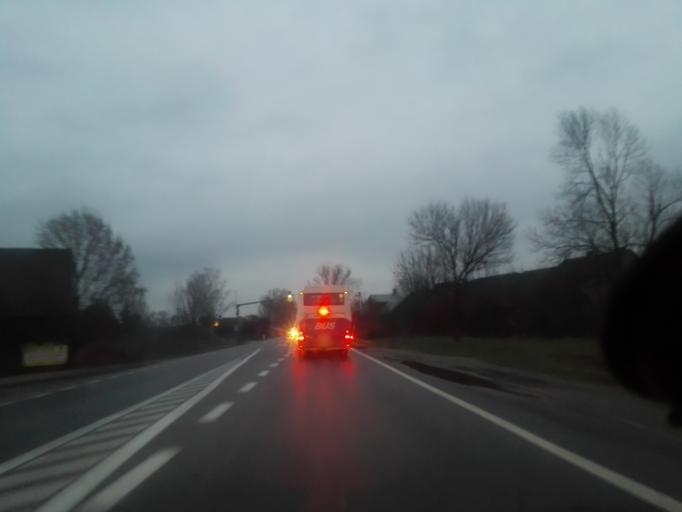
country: PL
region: Masovian Voivodeship
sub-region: Powiat wyszkowski
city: Branszczyk
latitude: 52.6477
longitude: 21.5527
